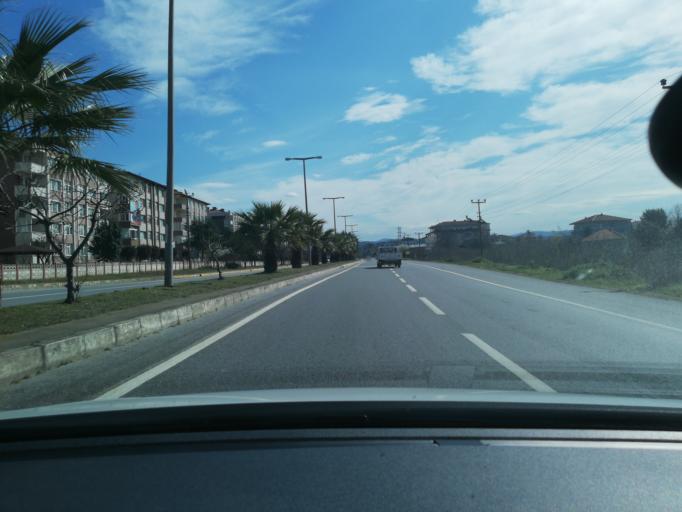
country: TR
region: Duzce
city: Akcakoca
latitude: 41.0856
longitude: 31.1661
